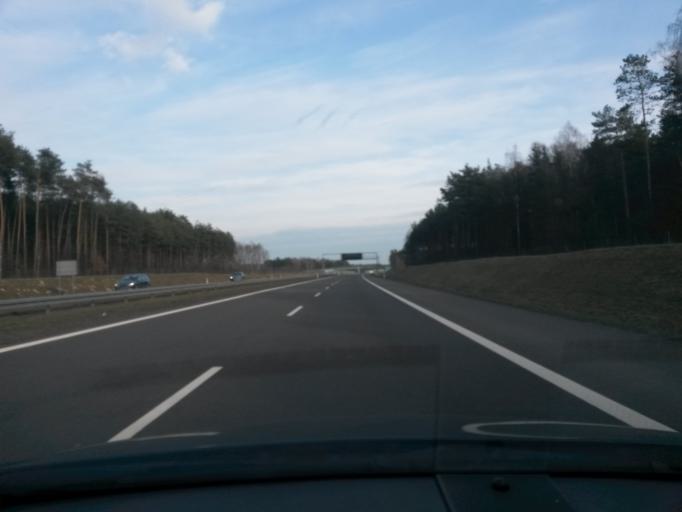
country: PL
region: Lodz Voivodeship
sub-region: Powiat zgierski
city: Zgierz
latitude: 51.9165
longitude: 19.4197
